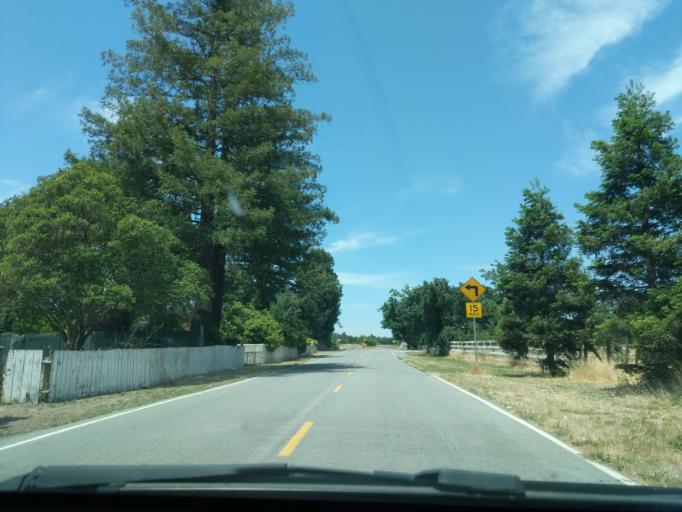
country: US
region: California
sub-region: Santa Clara County
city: Gilroy
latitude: 37.0516
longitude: -121.5578
